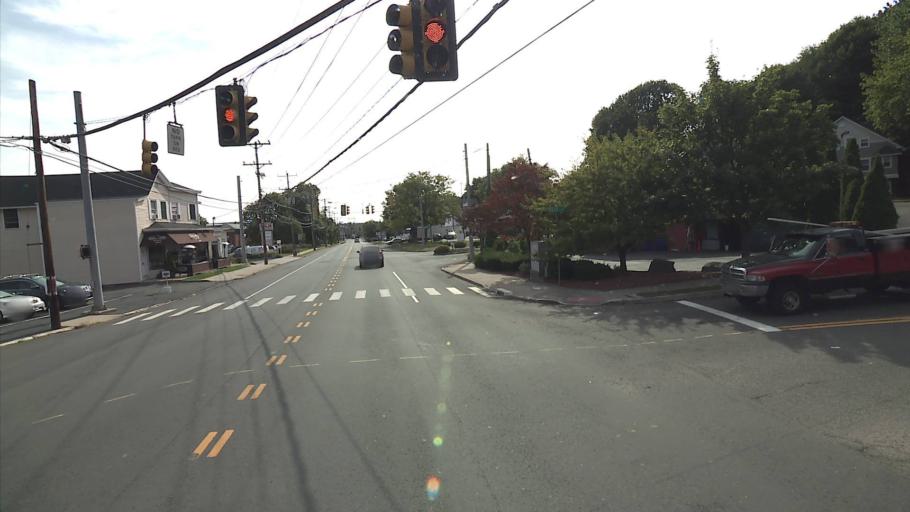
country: US
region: Connecticut
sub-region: Fairfield County
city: Norwalk
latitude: 41.1282
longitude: -73.4362
